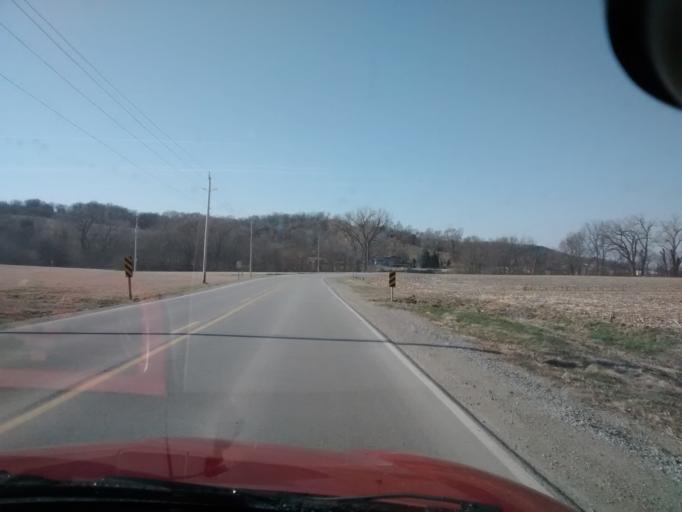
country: US
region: Iowa
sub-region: Pottawattamie County
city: Carter Lake
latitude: 41.3881
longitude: -95.8430
